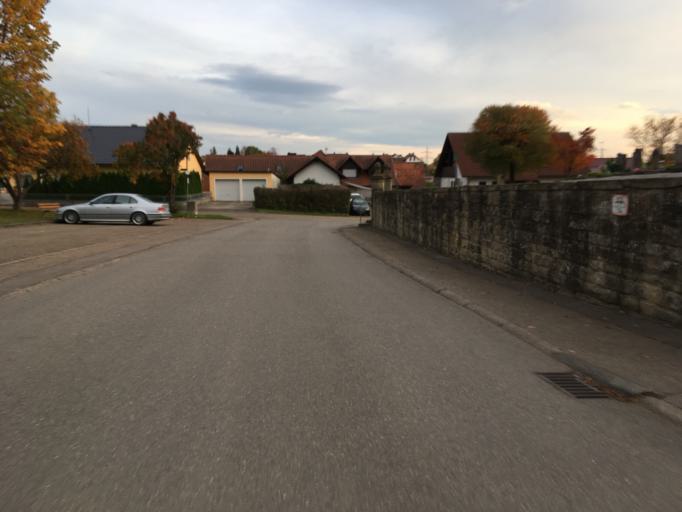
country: DE
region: Baden-Wuerttemberg
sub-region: Regierungsbezirk Stuttgart
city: Kirchardt
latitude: 49.2281
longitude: 8.9948
